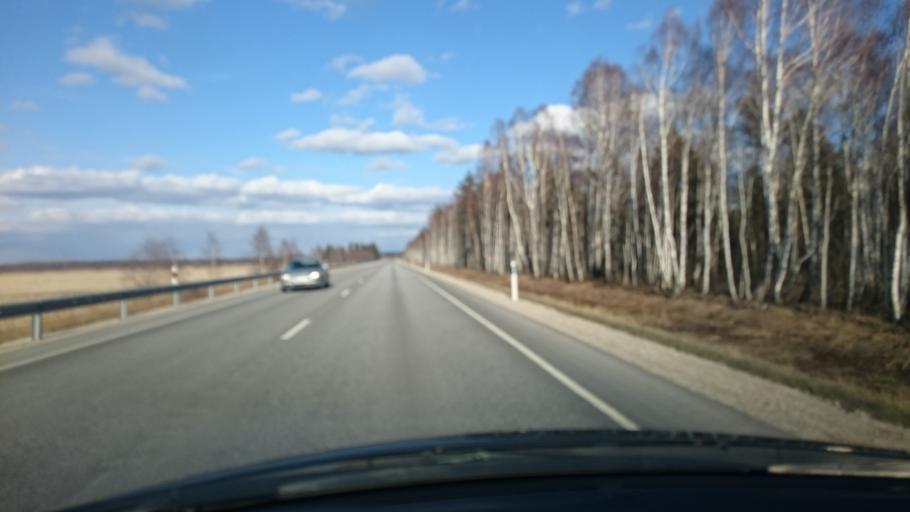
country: EE
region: Laeaene
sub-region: Lihula vald
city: Lihula
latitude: 58.7869
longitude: 24.0180
